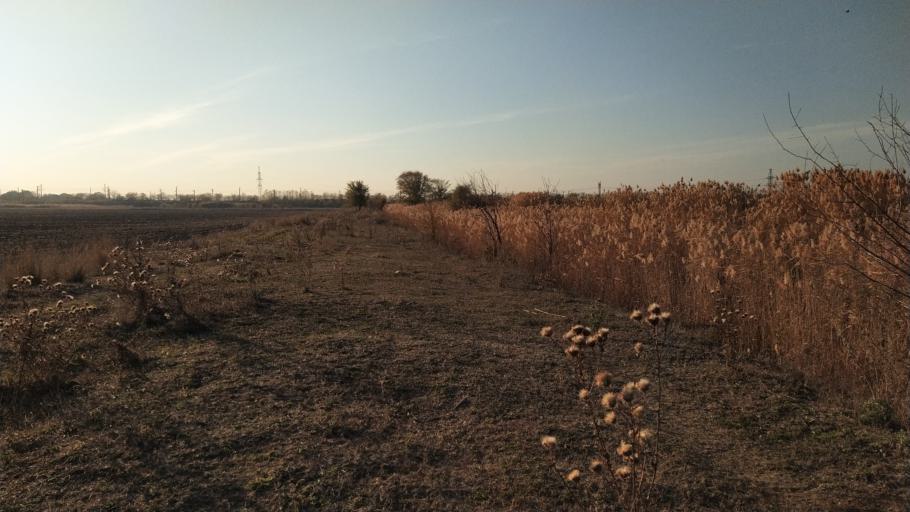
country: RU
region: Rostov
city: Bataysk
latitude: 47.1215
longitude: 39.7198
